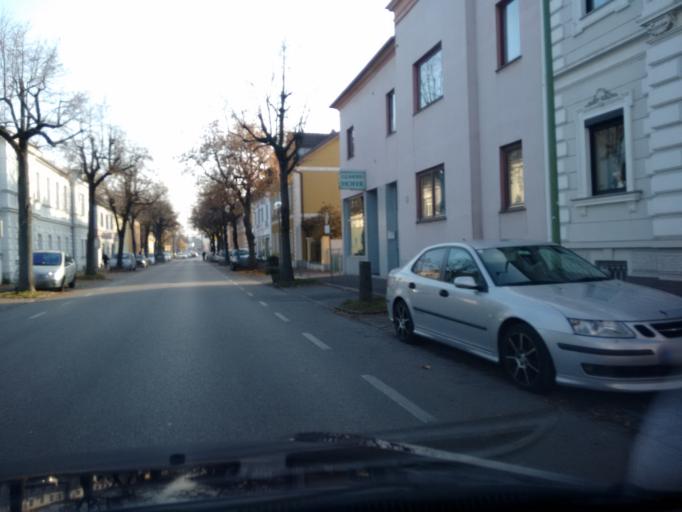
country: AT
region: Upper Austria
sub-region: Wels Stadt
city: Wels
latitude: 48.1677
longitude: 14.0229
